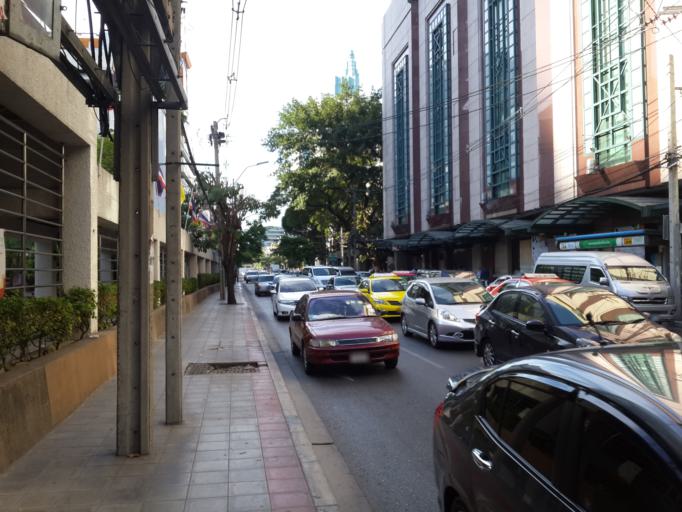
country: TH
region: Bangkok
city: Ratchathewi
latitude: 13.7443
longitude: 100.5441
